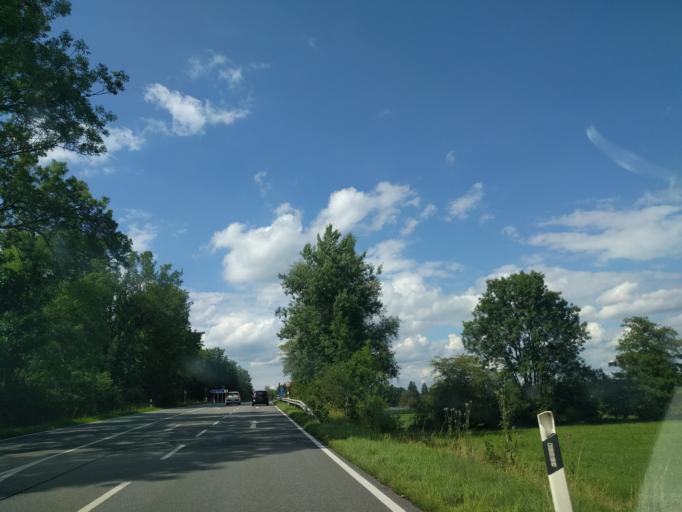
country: DE
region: Bavaria
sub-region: Upper Bavaria
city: Bad Feilnbach
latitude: 47.8180
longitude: 12.0148
